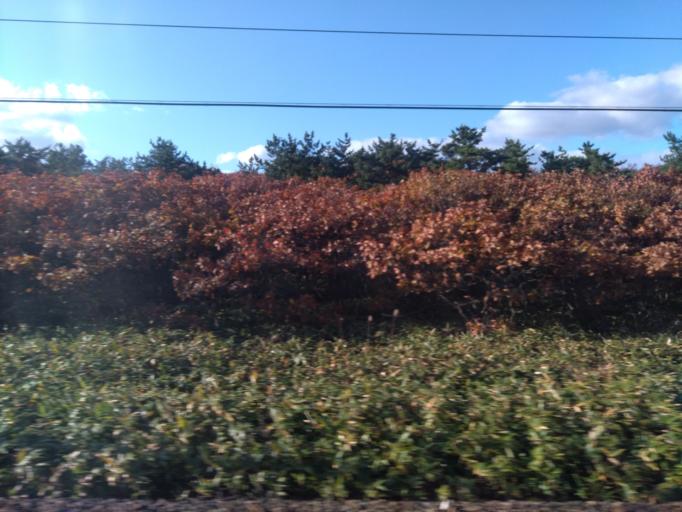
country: JP
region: Hokkaido
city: Niseko Town
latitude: 42.5566
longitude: 140.4251
